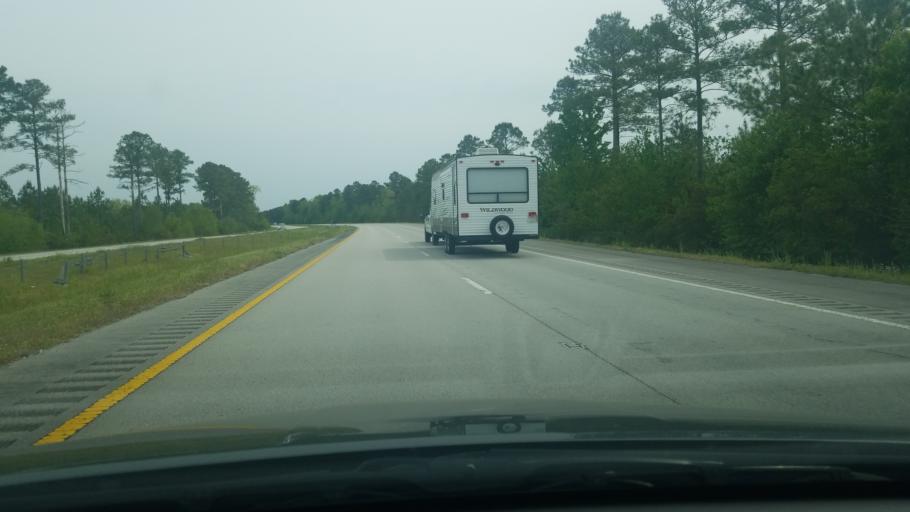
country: US
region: North Carolina
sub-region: Craven County
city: River Bend
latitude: 35.1071
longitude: -77.1639
